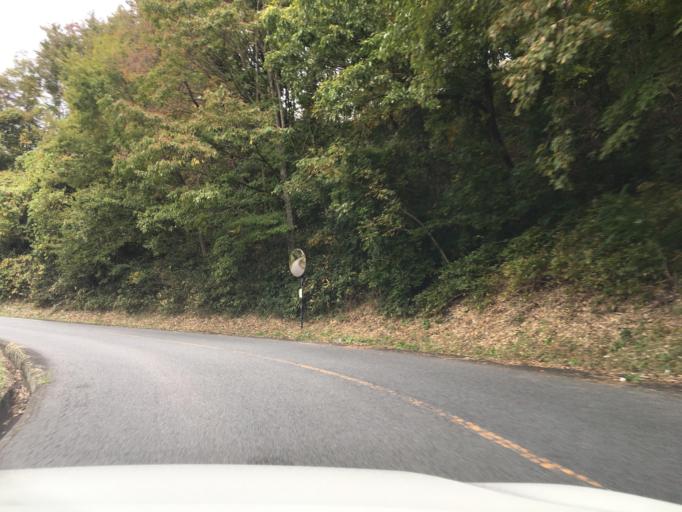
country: JP
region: Fukushima
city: Miharu
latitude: 37.4568
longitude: 140.5049
